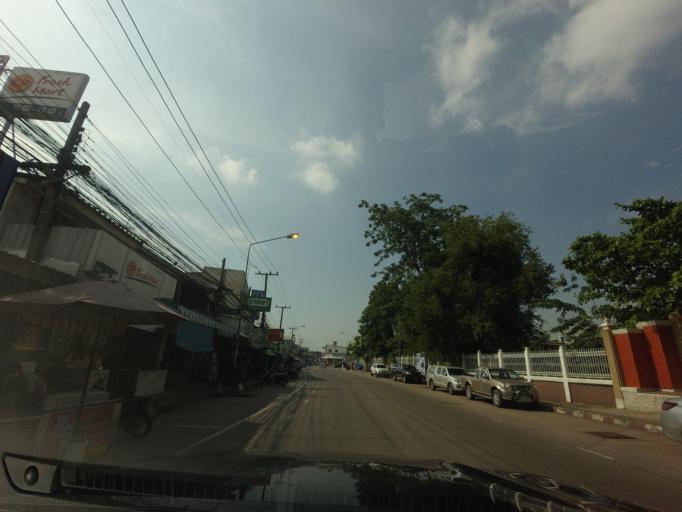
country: TH
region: Khon Kaen
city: Khon Kaen
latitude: 16.4209
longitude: 102.8497
